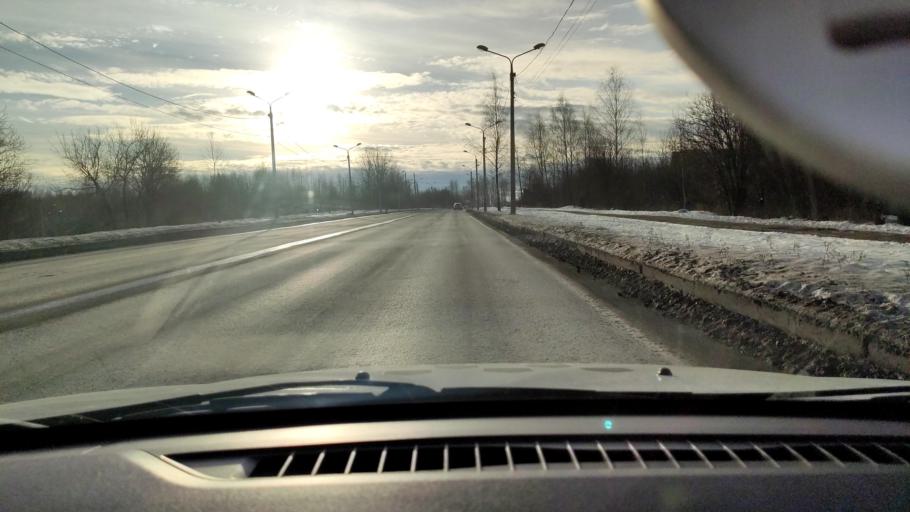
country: RU
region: Perm
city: Perm
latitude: 58.0689
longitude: 56.3665
